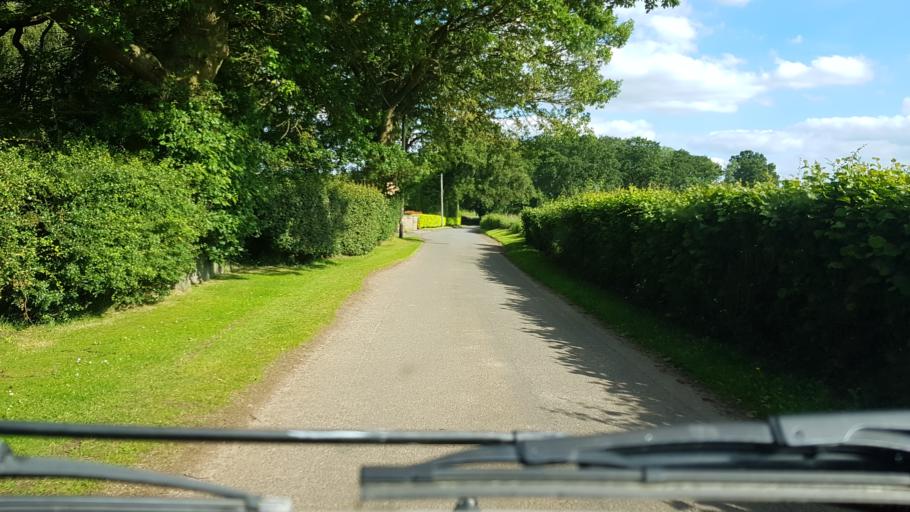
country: GB
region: England
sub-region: Worcestershire
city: Bewdley
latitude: 52.3382
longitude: -2.3230
